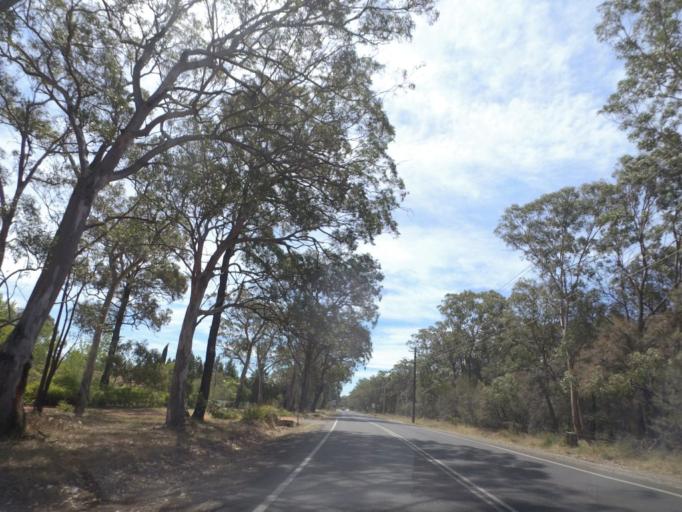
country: AU
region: New South Wales
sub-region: Wollondilly
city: Buxton
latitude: -34.3082
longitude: 150.5927
